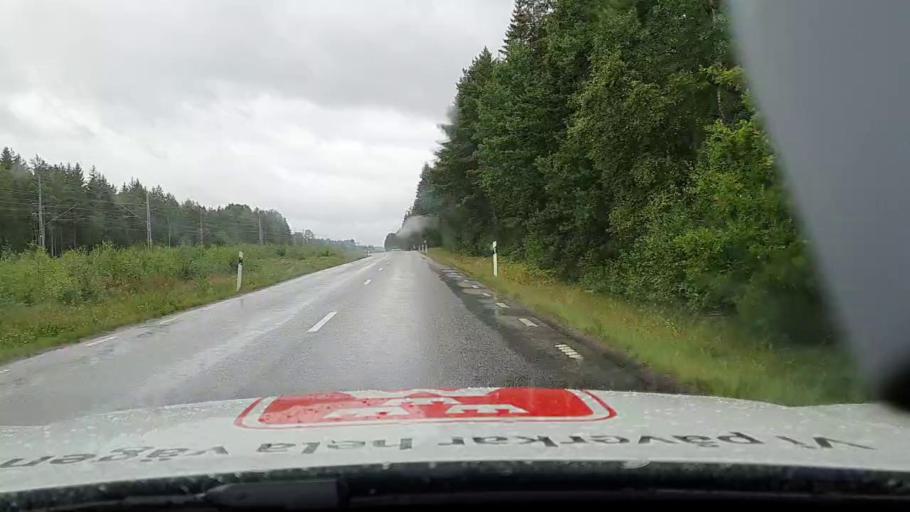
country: SE
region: Vaestra Goetaland
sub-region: Toreboda Kommun
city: Toereboda
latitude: 58.6670
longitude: 14.0928
